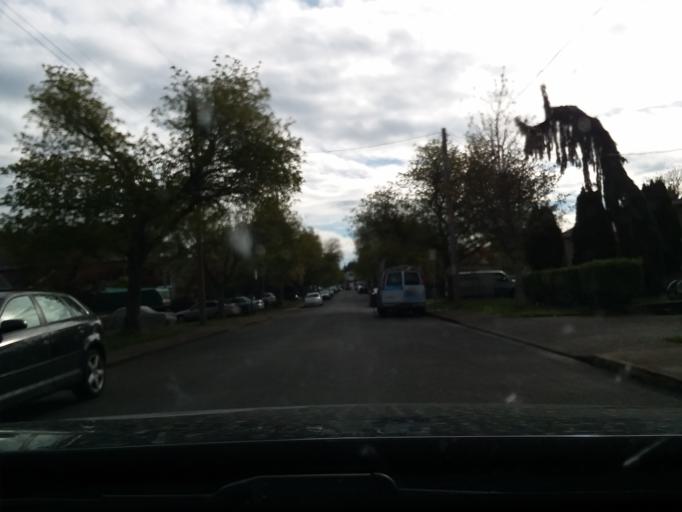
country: CA
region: British Columbia
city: Oak Bay
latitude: 48.4369
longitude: -123.3317
